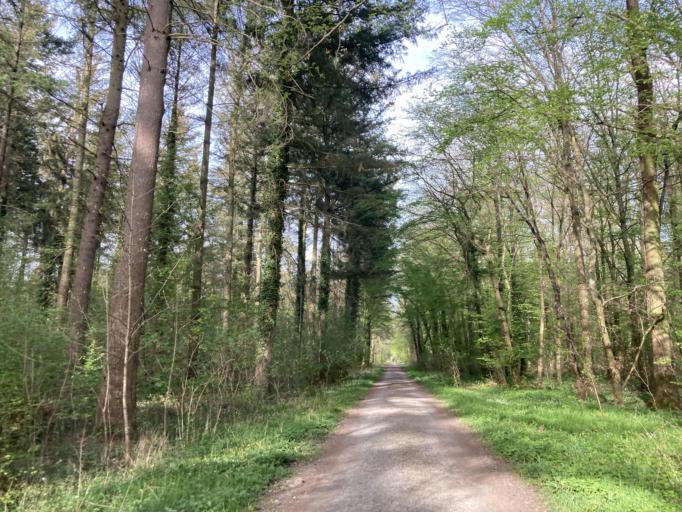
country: DE
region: Baden-Wuerttemberg
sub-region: Karlsruhe Region
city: Bruchsal
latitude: 49.1070
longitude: 8.5615
